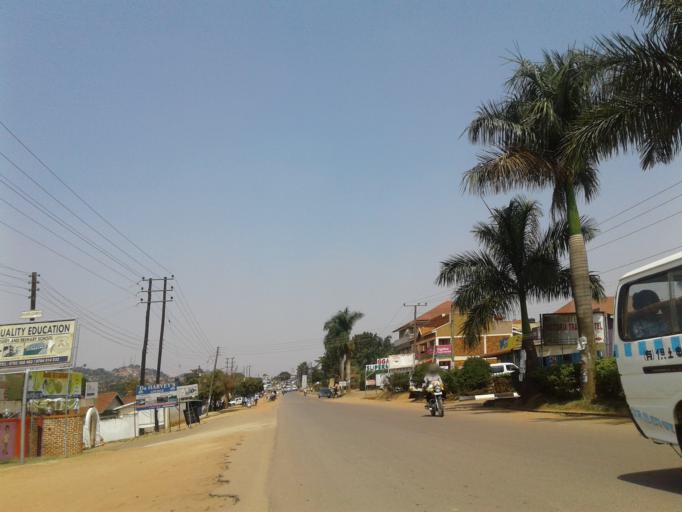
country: UG
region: Central Region
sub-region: Kampala District
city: Kampala
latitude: 0.2564
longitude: 32.6304
